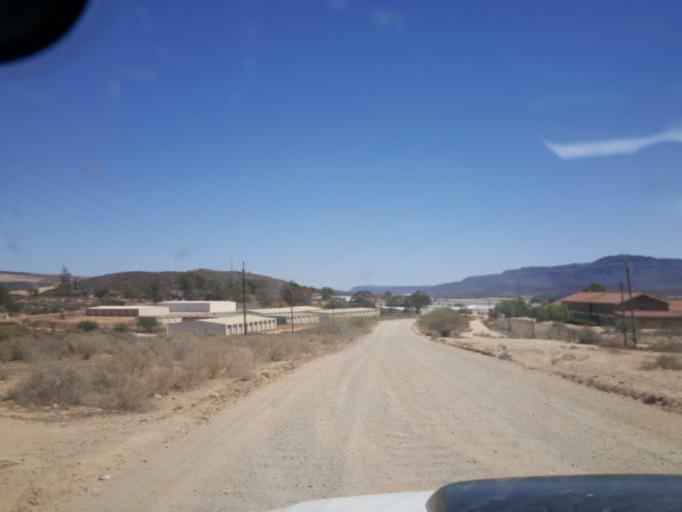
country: ZA
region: Western Cape
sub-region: West Coast District Municipality
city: Clanwilliam
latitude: -32.1931
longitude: 18.8896
